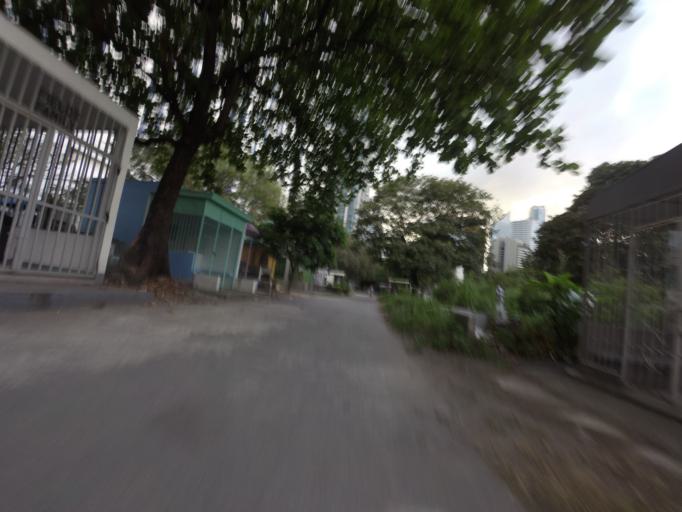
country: PH
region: Metro Manila
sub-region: Makati City
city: Makati City
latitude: 14.5645
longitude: 121.0211
